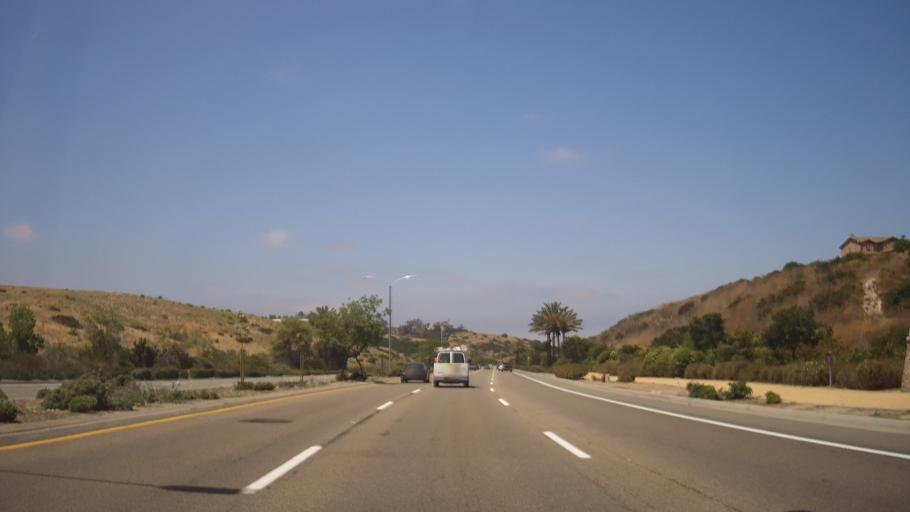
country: US
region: California
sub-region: San Diego County
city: Bonita
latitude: 32.6113
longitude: -117.0128
